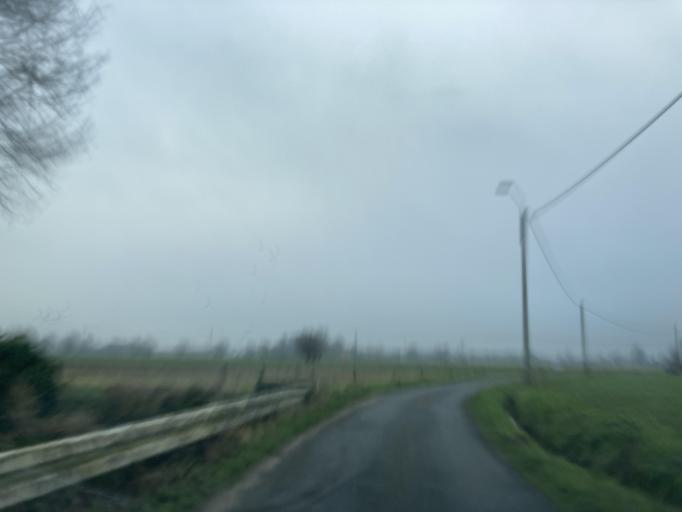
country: BE
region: Flanders
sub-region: Provincie West-Vlaanderen
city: Ichtegem
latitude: 51.1420
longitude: 3.0381
